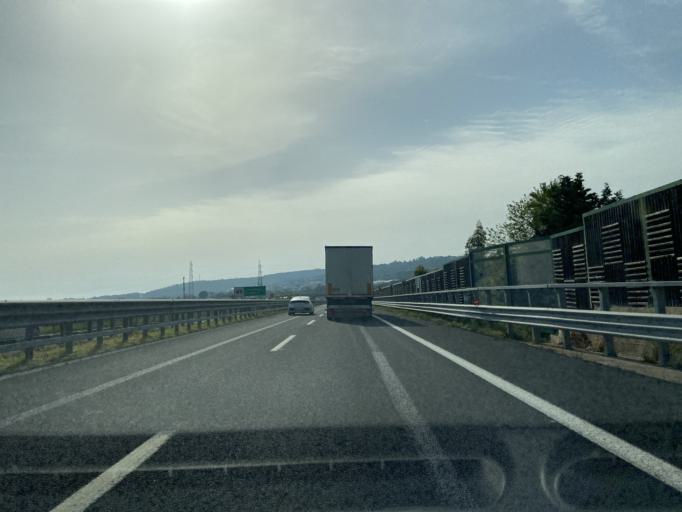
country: IT
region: Latium
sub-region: Citta metropolitana di Roma Capitale
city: Santa Marinella
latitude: 42.0444
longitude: 11.8982
